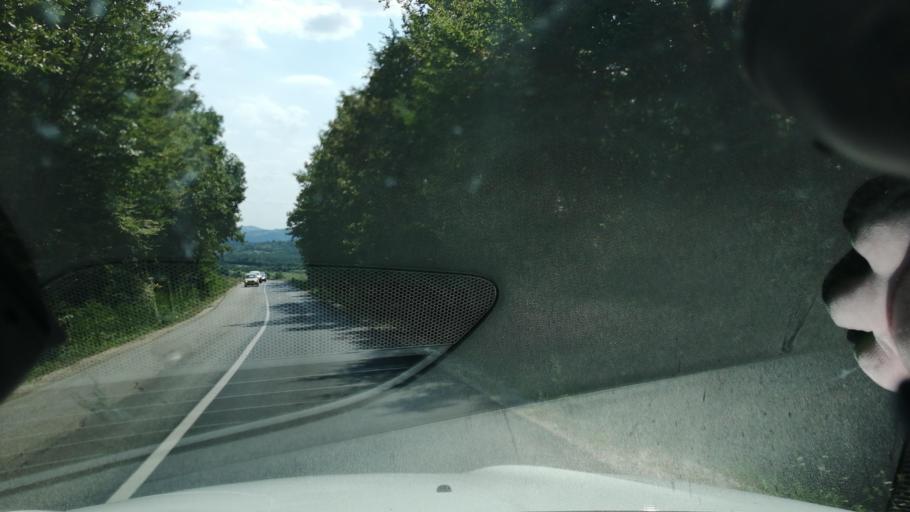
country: RS
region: Central Serbia
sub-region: Moravicki Okrug
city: Cacak
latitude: 43.8132
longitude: 20.2756
